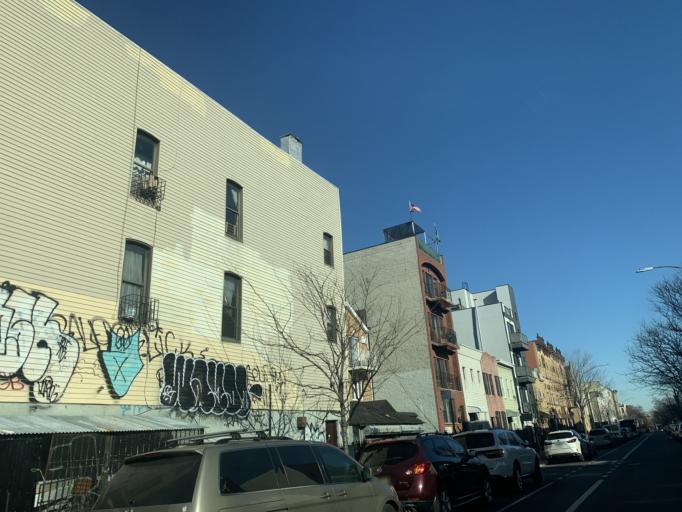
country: US
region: New York
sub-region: Kings County
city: East New York
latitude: 40.6949
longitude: -73.9249
